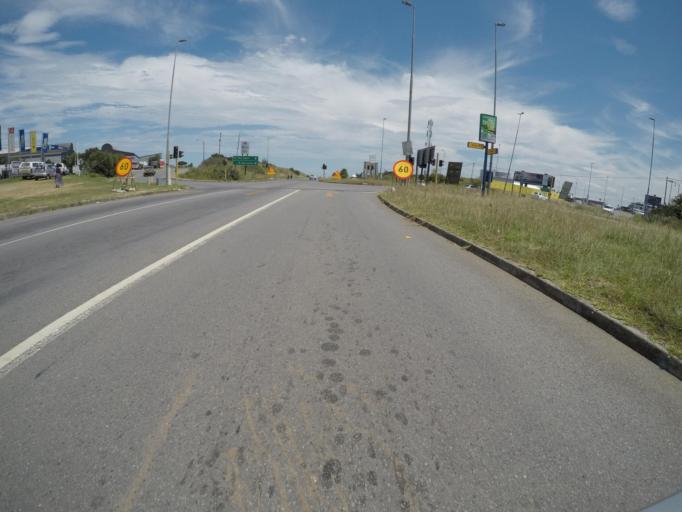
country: ZA
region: Eastern Cape
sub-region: Buffalo City Metropolitan Municipality
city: East London
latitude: -33.0381
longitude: 27.8328
